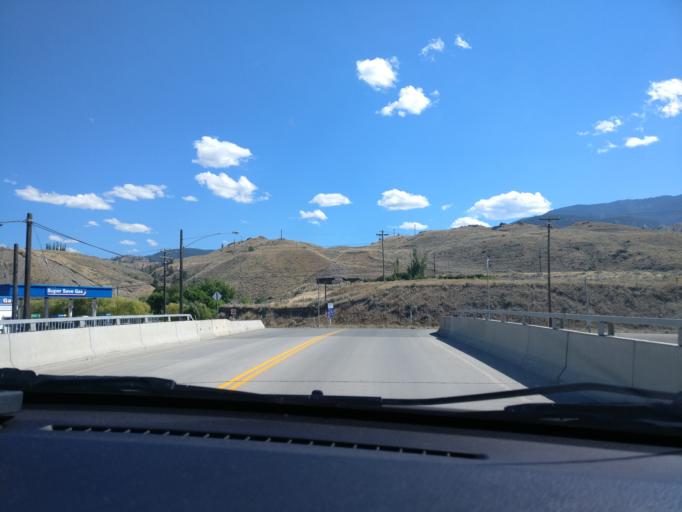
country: CA
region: British Columbia
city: Logan Lake
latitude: 50.7601
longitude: -120.8129
